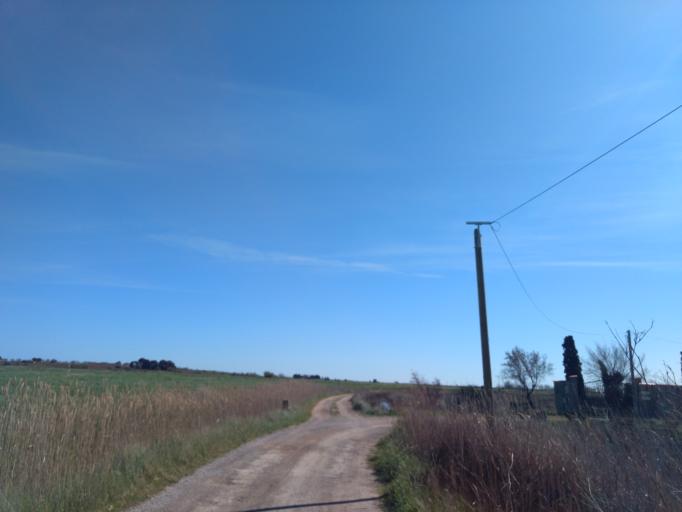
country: FR
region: Languedoc-Roussillon
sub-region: Departement de l'Herault
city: Mireval
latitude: 43.5180
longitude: 3.8345
